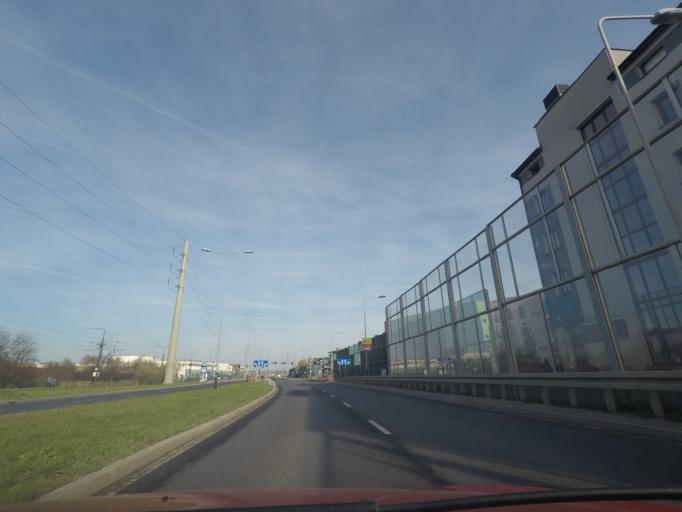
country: PL
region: Lesser Poland Voivodeship
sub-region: Krakow
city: Sidzina
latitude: 50.0230
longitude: 19.9011
